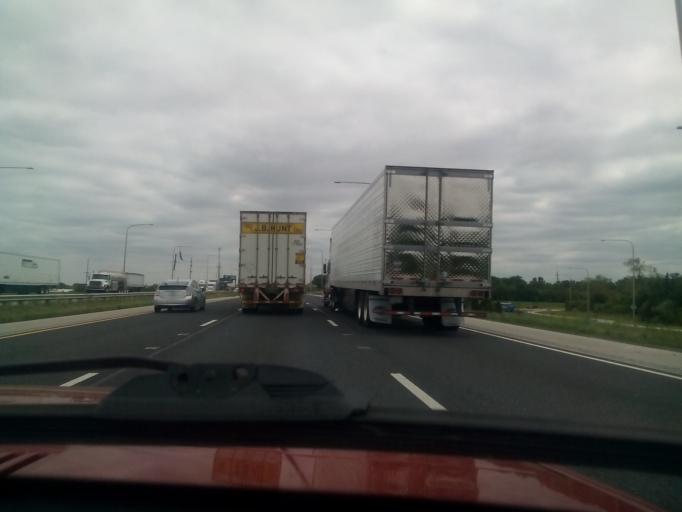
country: US
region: Illinois
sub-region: Cook County
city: Markham
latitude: 41.5829
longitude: -87.6977
